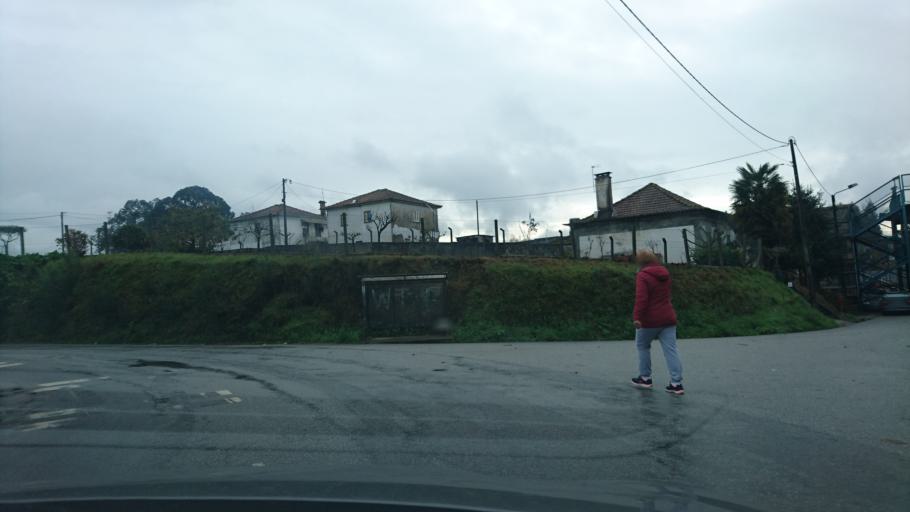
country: PT
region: Porto
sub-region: Paredes
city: Recarei
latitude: 41.1533
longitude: -8.3967
